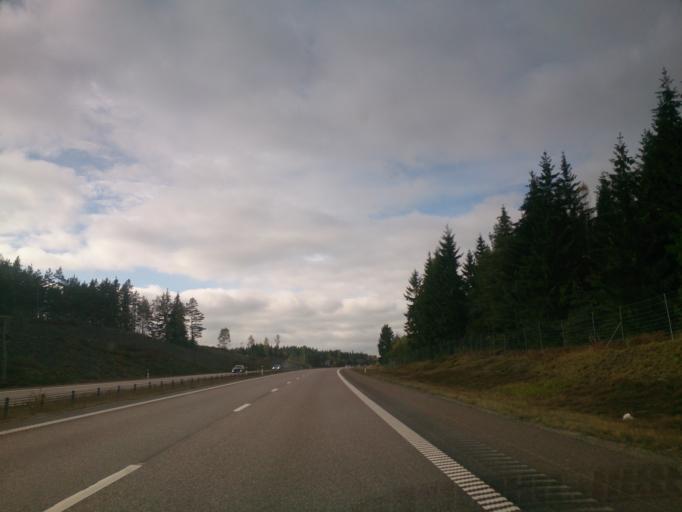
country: SE
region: OEstergoetland
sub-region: Norrkopings Kommun
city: Krokek
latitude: 58.7265
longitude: 16.4008
